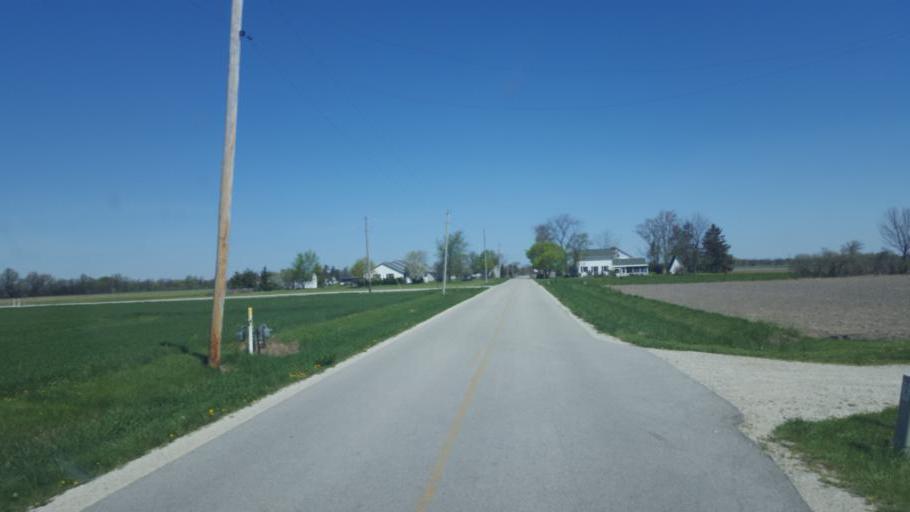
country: US
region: Ohio
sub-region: Ottawa County
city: Oak Harbor
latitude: 41.4857
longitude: -83.1259
